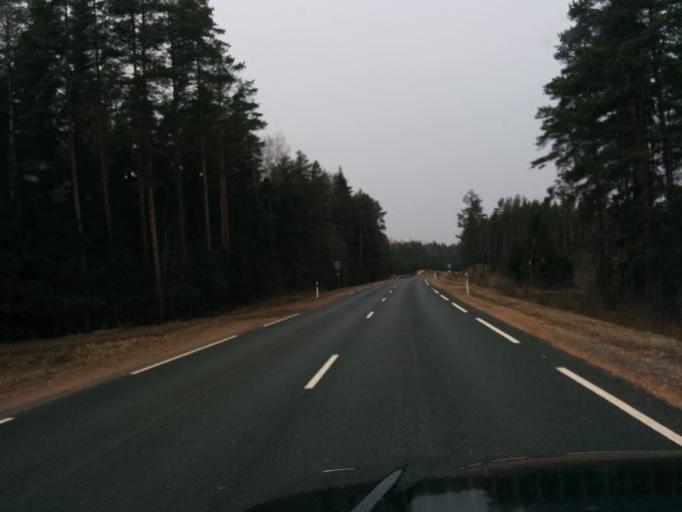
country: LV
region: Ikskile
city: Ikskile
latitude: 56.8021
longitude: 24.5068
